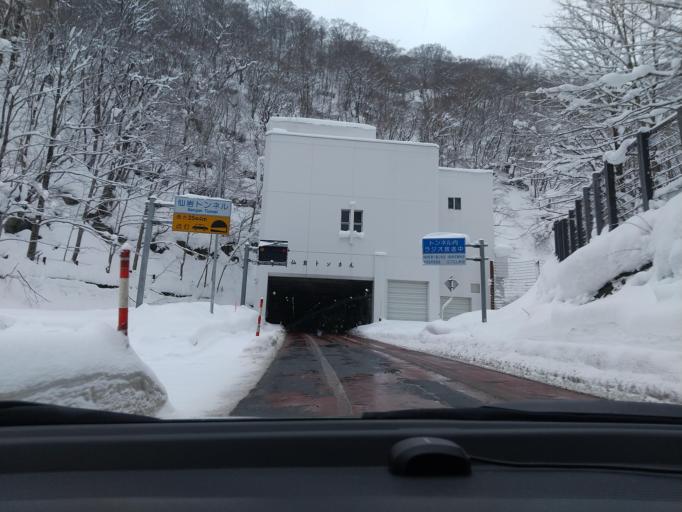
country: JP
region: Iwate
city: Shizukuishi
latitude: 39.6972
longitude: 140.8005
